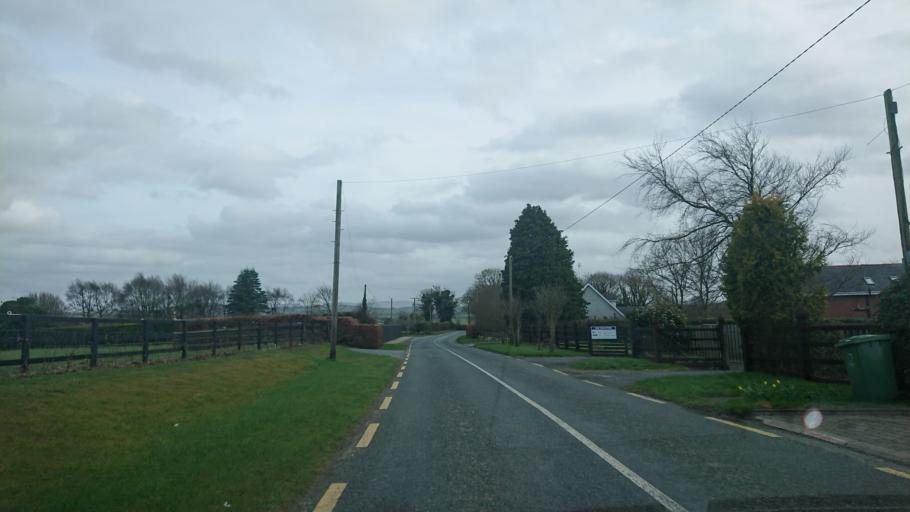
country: IE
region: Leinster
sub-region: Kildare
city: Naas
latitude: 53.1913
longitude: -6.6464
